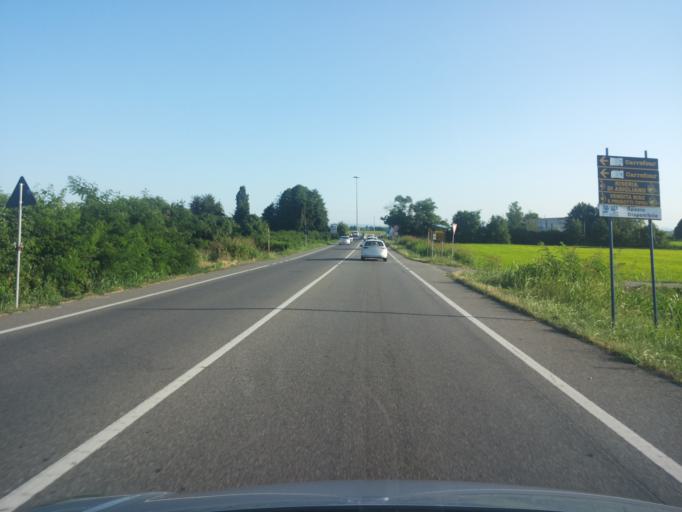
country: IT
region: Piedmont
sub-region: Provincia di Vercelli
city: Caresanablot
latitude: 45.3264
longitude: 8.3888
